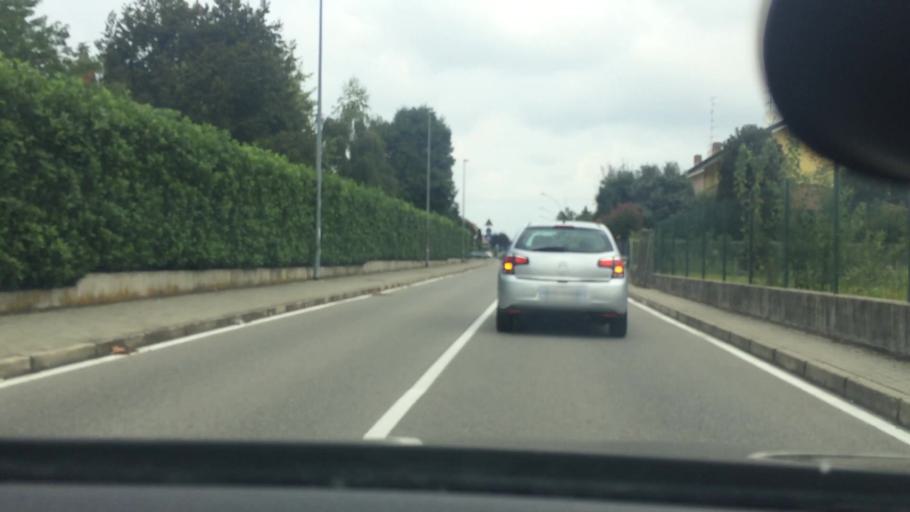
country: IT
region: Lombardy
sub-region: Provincia di Monza e Brianza
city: Ceriano Laghetto
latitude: 45.6362
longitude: 9.0754
